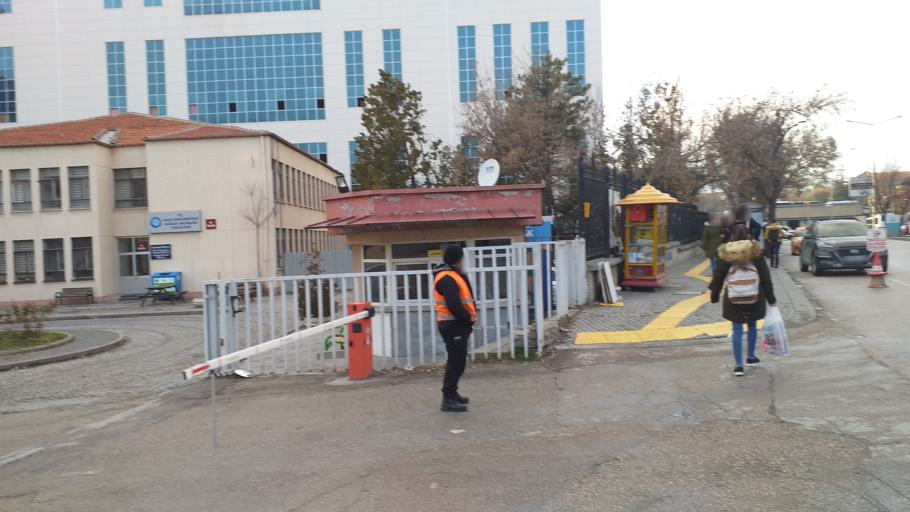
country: TR
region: Ankara
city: Ankara
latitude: 39.9355
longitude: 32.8249
